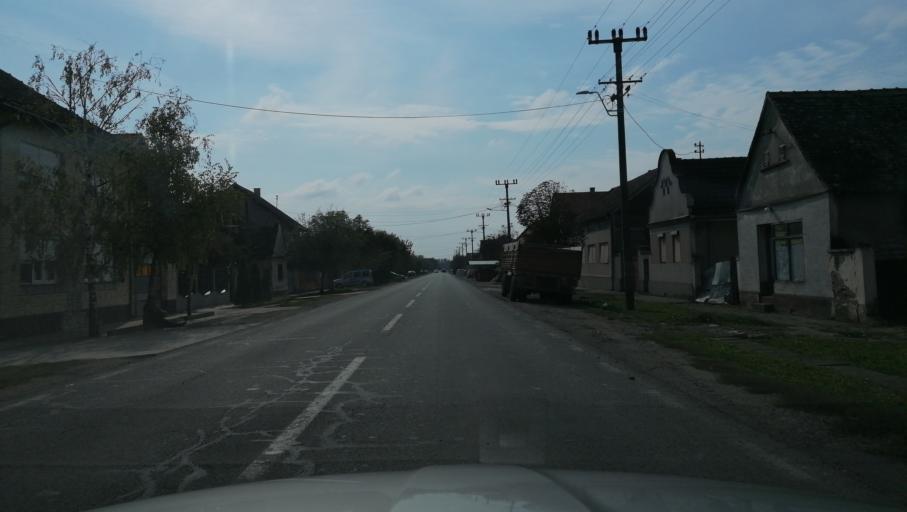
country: RS
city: Ravnje
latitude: 45.0226
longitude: 19.4033
